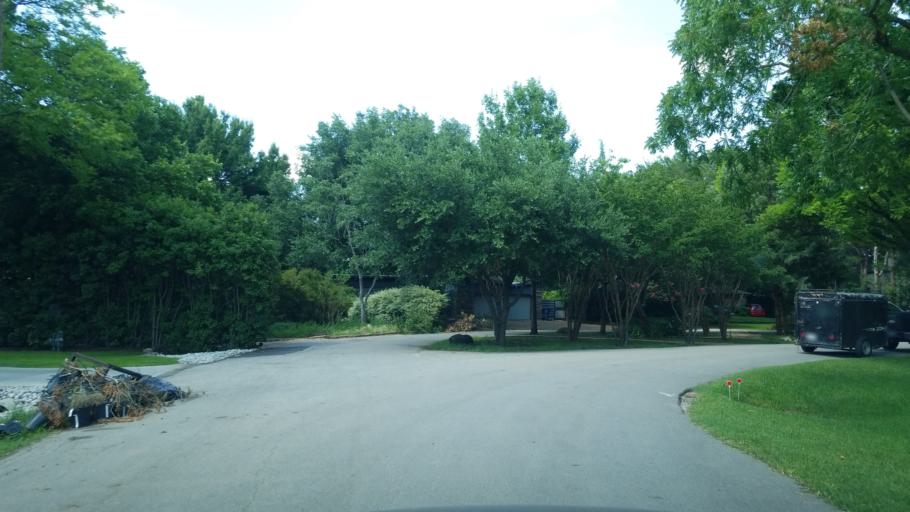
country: US
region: Texas
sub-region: Dallas County
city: University Park
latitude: 32.8855
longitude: -96.8371
